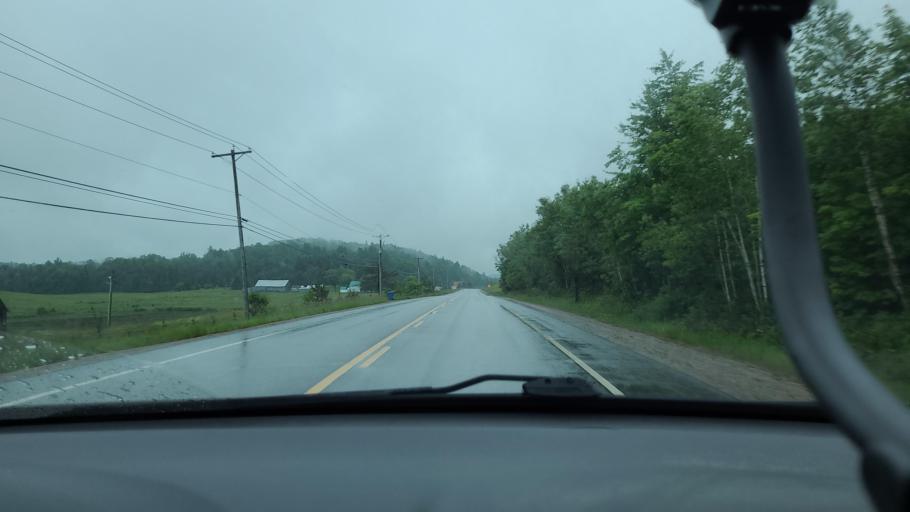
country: CA
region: Quebec
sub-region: Outaouais
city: Saint-Andre-Avellin
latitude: 45.8601
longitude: -75.0490
